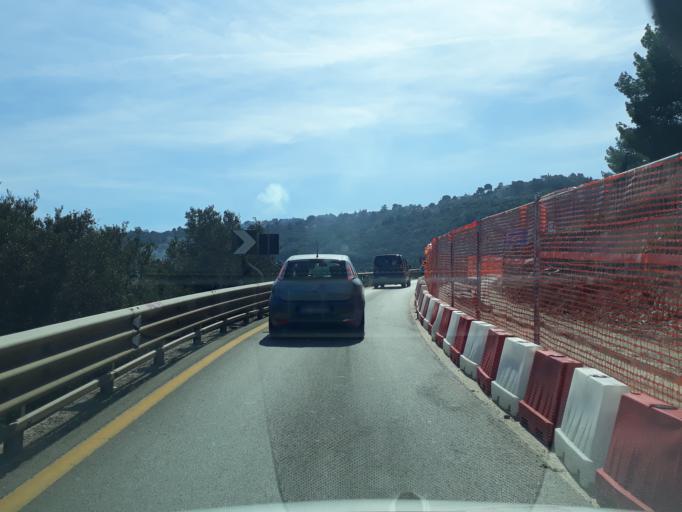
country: IT
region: Apulia
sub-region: Provincia di Brindisi
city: Lamie di Olimpie-Selva
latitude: 40.8131
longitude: 17.3466
